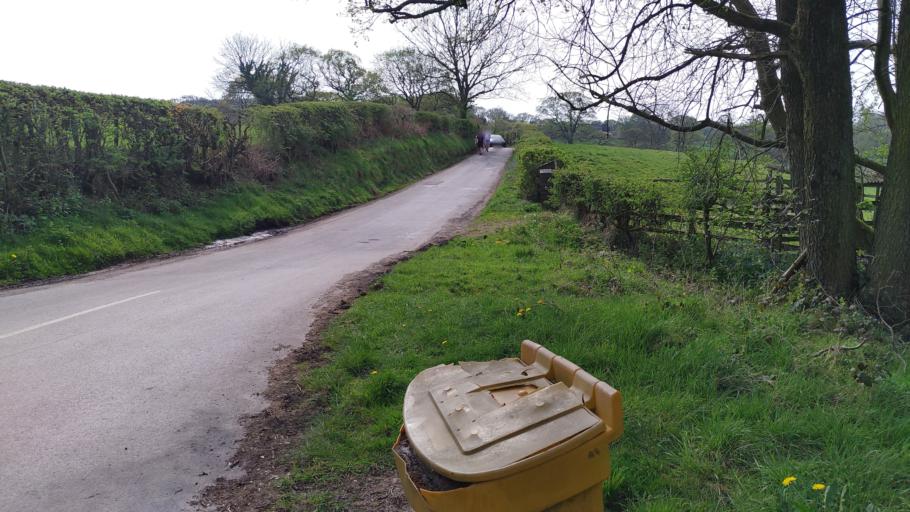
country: GB
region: England
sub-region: Lancashire
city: Chorley
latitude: 53.6668
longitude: -2.5848
